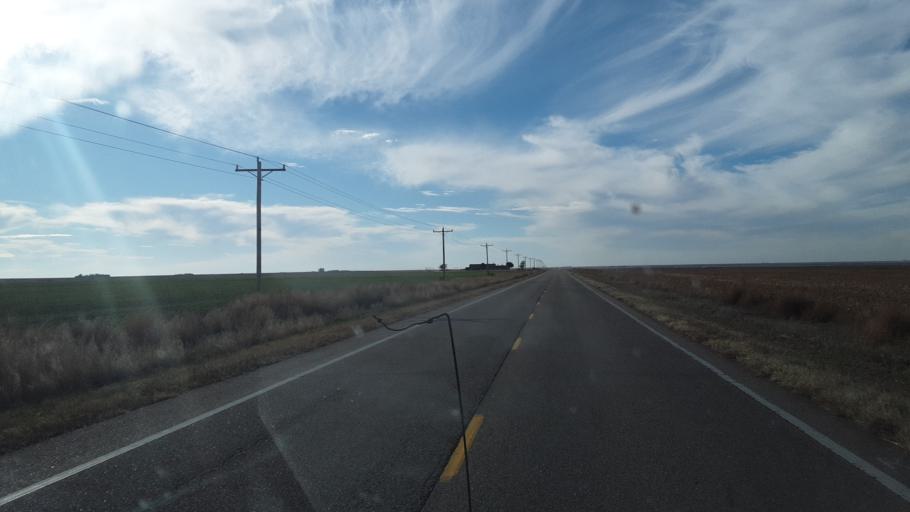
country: US
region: Kansas
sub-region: Gray County
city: Cimarron
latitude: 38.0592
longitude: -100.4926
